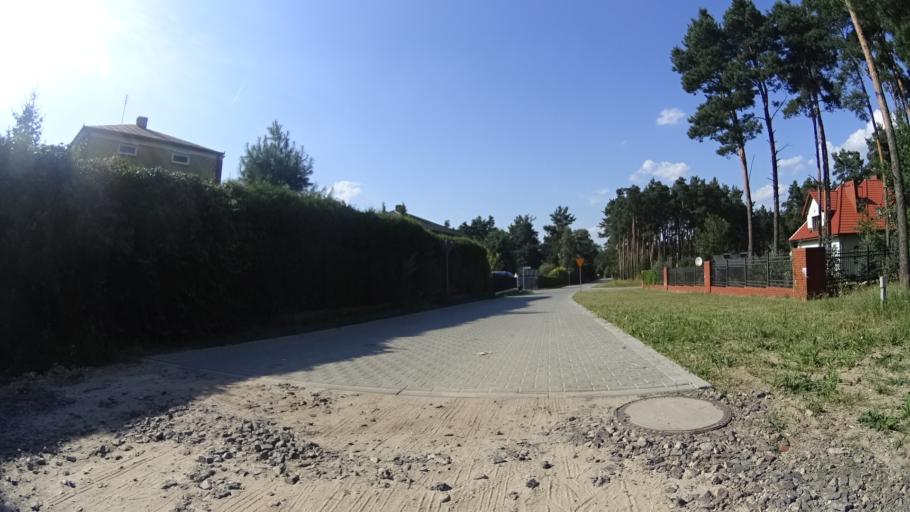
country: PL
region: Masovian Voivodeship
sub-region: Powiat bialobrzeski
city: Wysmierzyce
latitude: 51.6261
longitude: 20.8269
